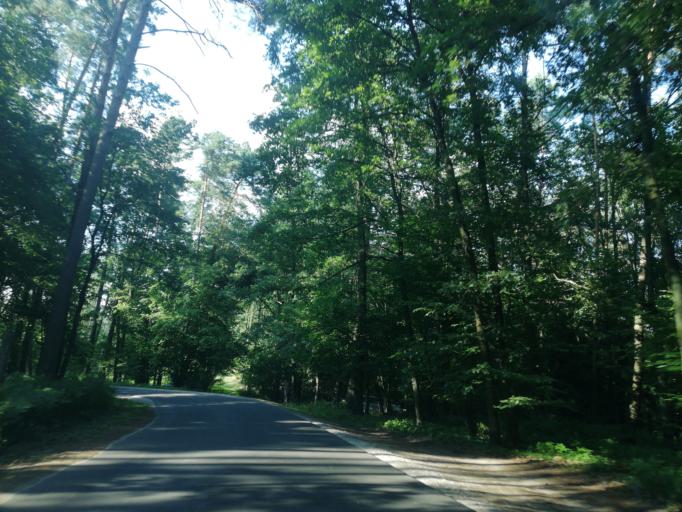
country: PL
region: Kujawsko-Pomorskie
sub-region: Powiat golubsko-dobrzynski
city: Ciechocin
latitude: 53.0790
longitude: 18.9500
